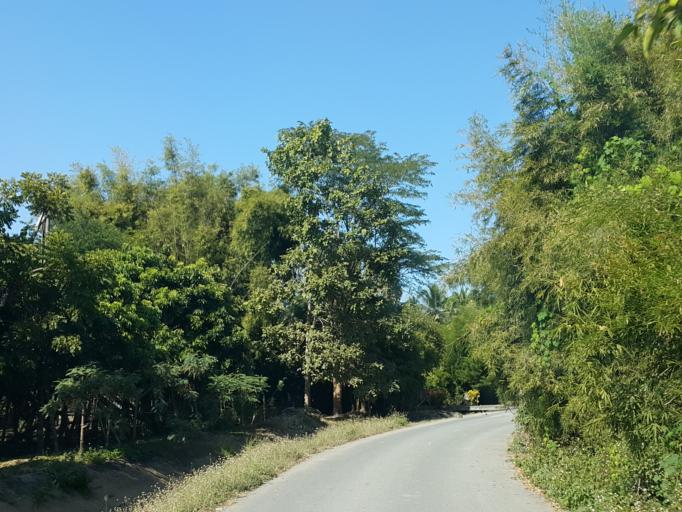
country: TH
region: Chiang Mai
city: San Sai
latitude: 18.8775
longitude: 98.9825
